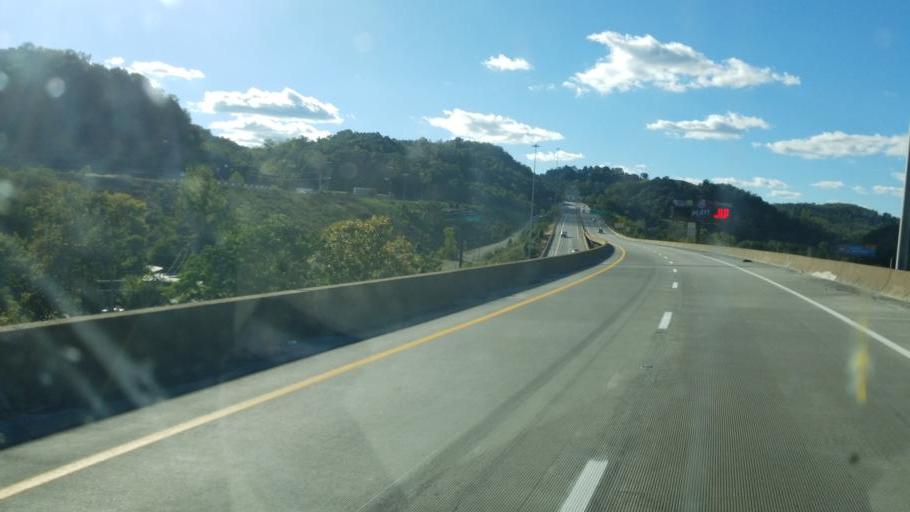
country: US
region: West Virginia
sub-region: Ohio County
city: Bethlehem
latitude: 40.0492
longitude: -80.6641
